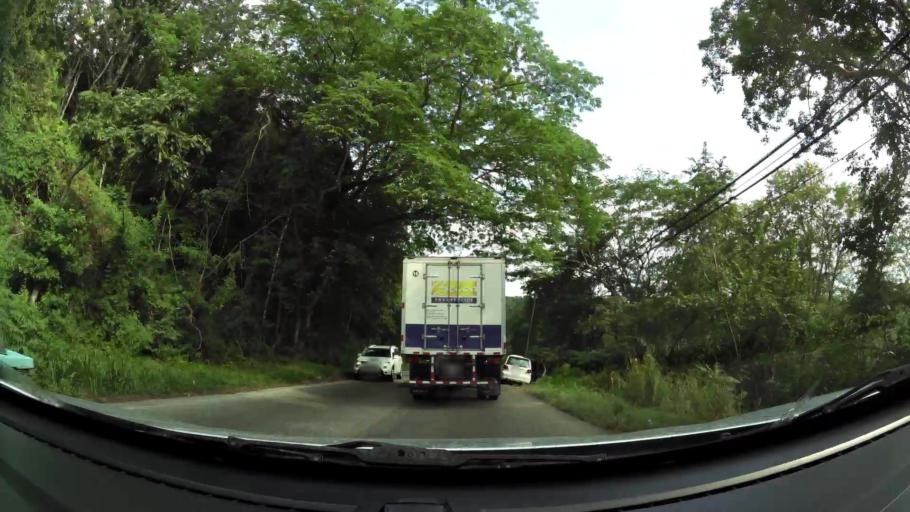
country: CR
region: Guanacaste
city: Juntas
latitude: 10.1906
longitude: -84.9479
